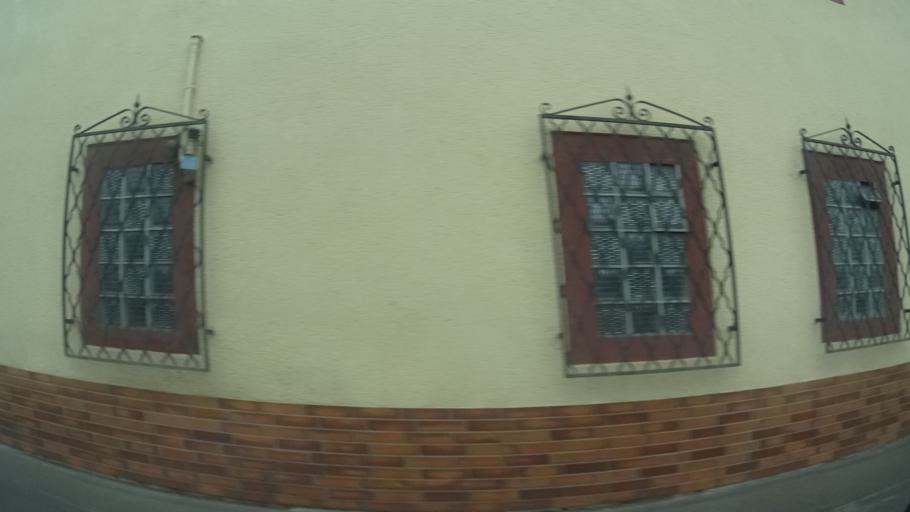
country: DE
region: Hesse
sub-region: Regierungsbezirk Darmstadt
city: Bad Soden-Salmunster
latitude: 50.2713
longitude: 9.3794
